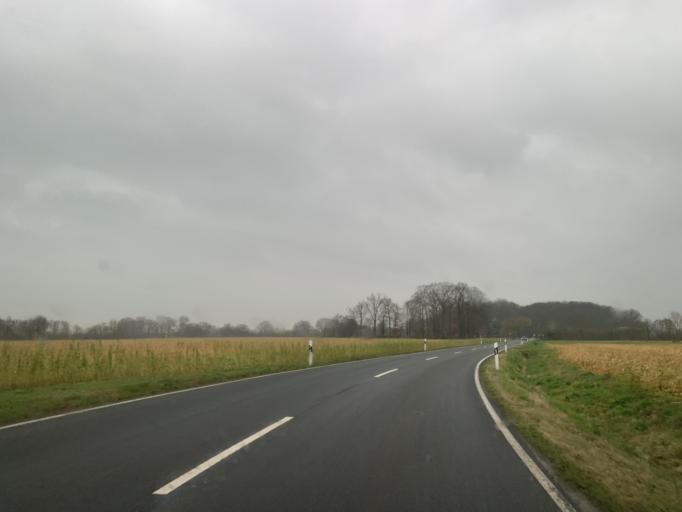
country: DE
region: North Rhine-Westphalia
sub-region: Regierungsbezirk Munster
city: Dulmen
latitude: 51.8442
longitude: 7.3506
